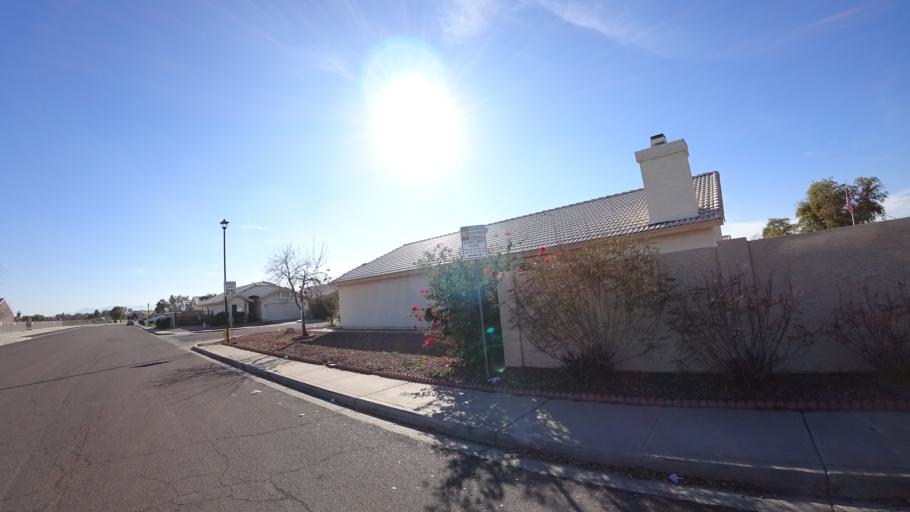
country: US
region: Arizona
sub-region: Maricopa County
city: Glendale
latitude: 33.5232
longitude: -112.2249
